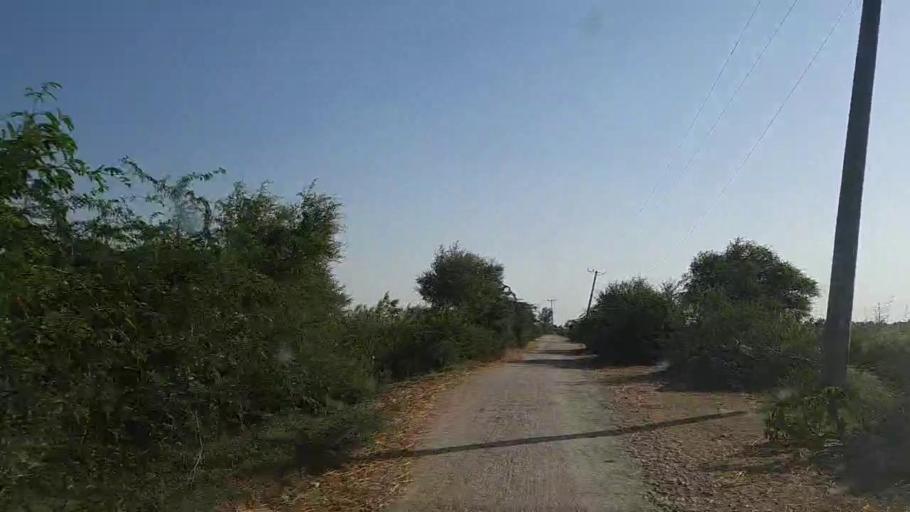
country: PK
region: Sindh
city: Thatta
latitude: 24.6366
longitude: 68.0763
